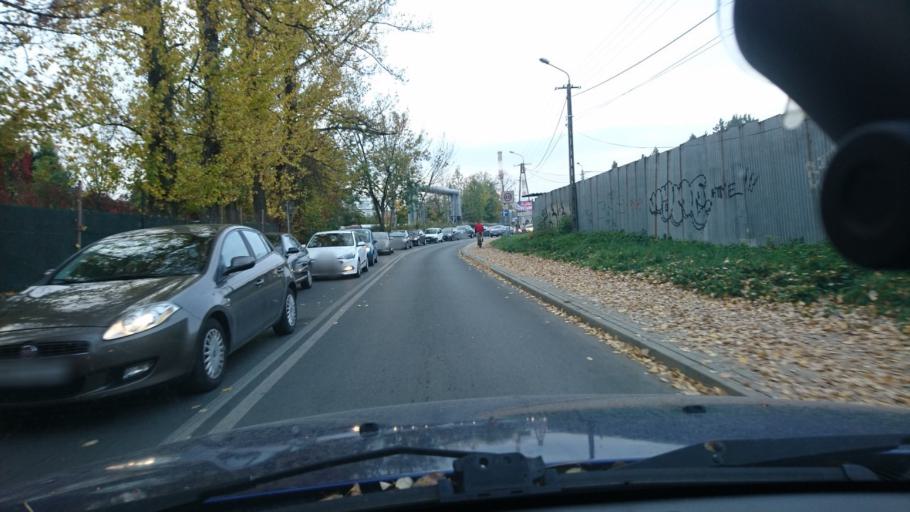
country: PL
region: Silesian Voivodeship
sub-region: Bielsko-Biala
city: Bielsko-Biala
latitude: 49.8192
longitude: 19.0599
